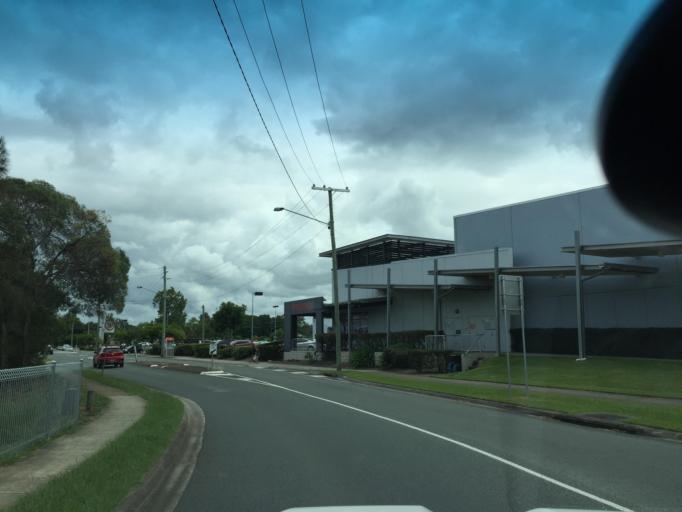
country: AU
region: Queensland
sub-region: Moreton Bay
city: Caboolture South
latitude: -27.0947
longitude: 152.9519
